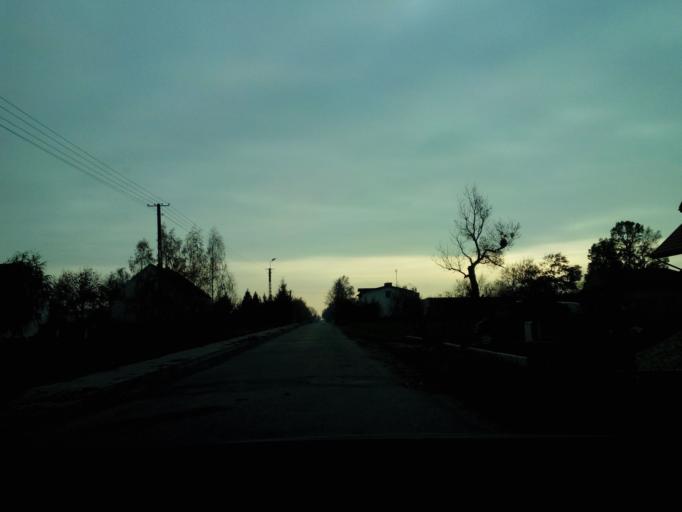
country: PL
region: Kujawsko-Pomorskie
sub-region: Powiat brodnicki
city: Swiedziebnia
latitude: 53.2037
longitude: 19.5713
